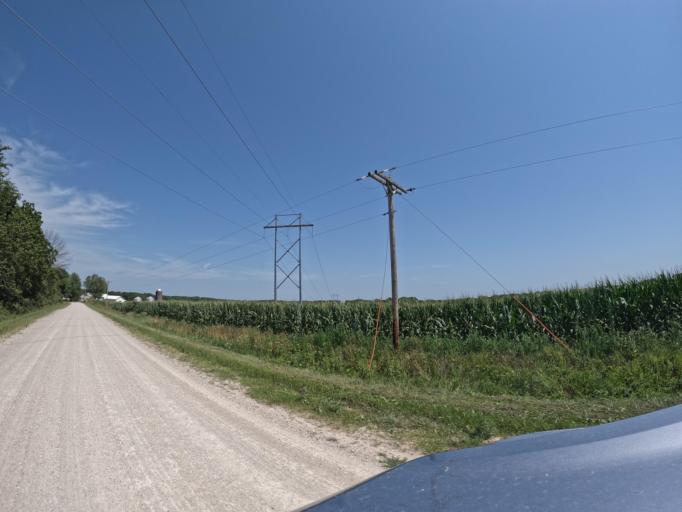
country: US
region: Iowa
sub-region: Henry County
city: Mount Pleasant
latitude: 40.9787
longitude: -91.6573
